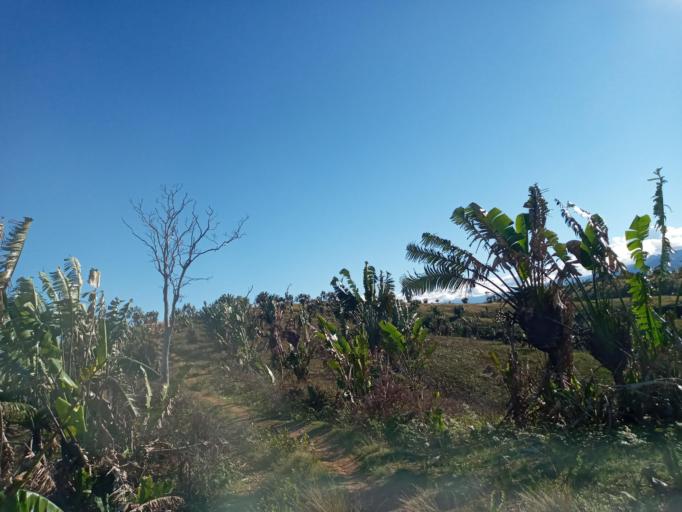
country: MG
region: Anosy
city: Fort Dauphin
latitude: -24.4064
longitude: 47.2476
